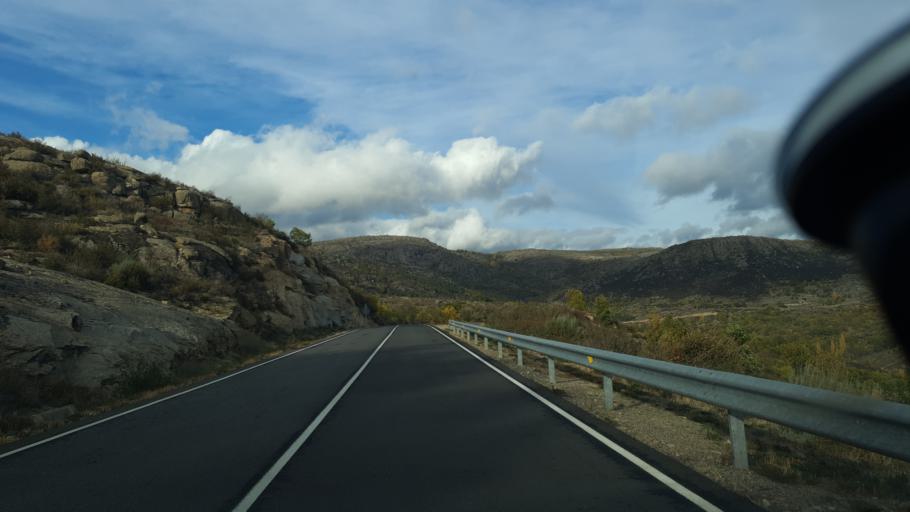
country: ES
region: Castille and Leon
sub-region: Provincia de Avila
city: Navalosa
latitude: 40.3992
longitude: -4.9067
